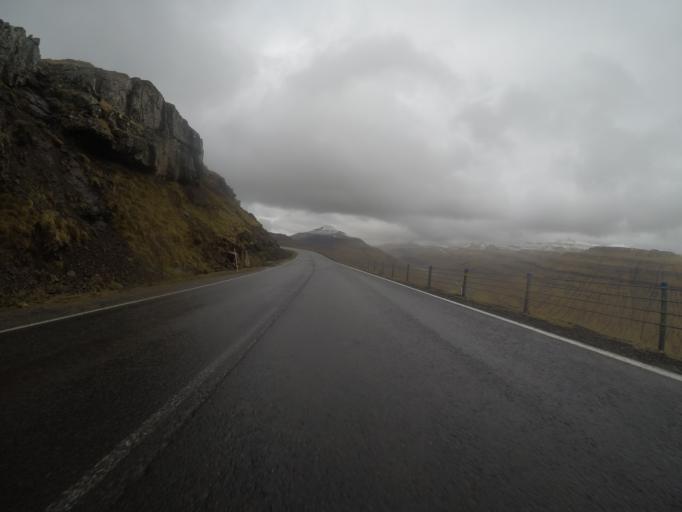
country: FO
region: Streymoy
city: Kollafjordhur
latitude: 62.0898
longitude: -6.9494
